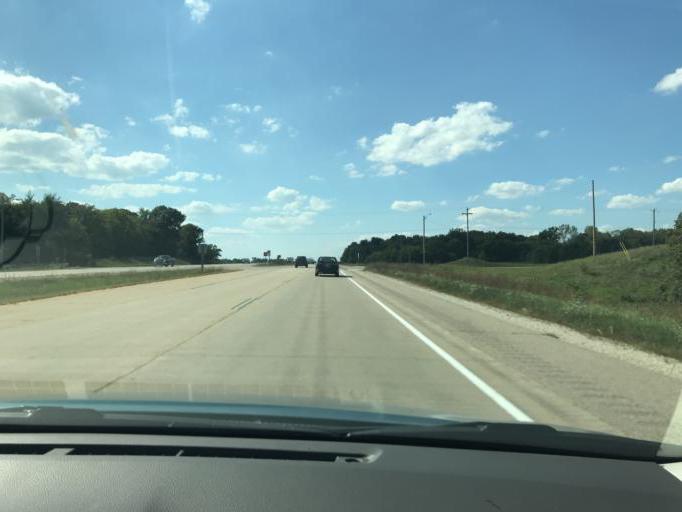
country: US
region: Wisconsin
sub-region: Kenosha County
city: Powers Lake
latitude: 42.5820
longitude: -88.2651
